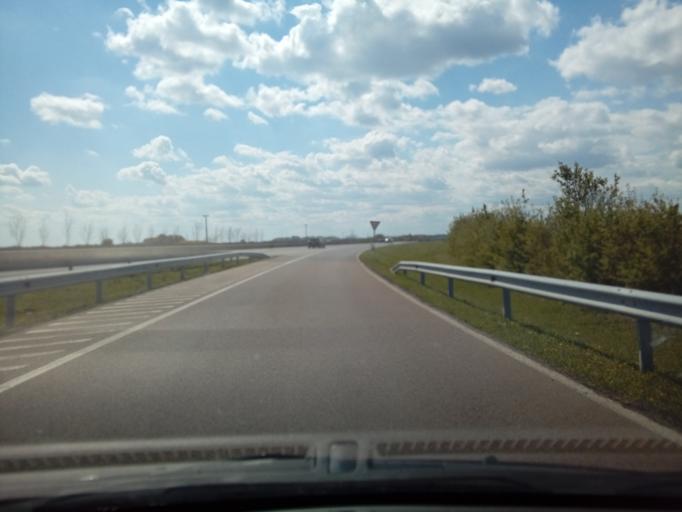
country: HU
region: Heves
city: Szihalom
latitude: 47.7656
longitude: 20.5125
